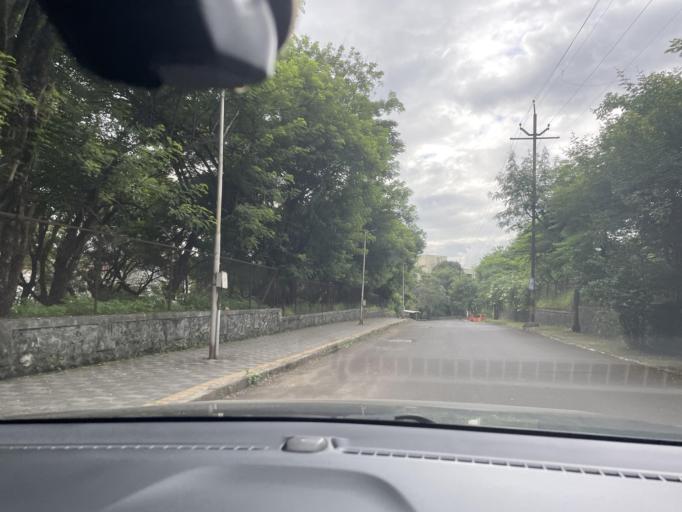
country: IN
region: Maharashtra
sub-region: Pune Division
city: Shivaji Nagar
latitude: 18.5327
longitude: 73.8130
